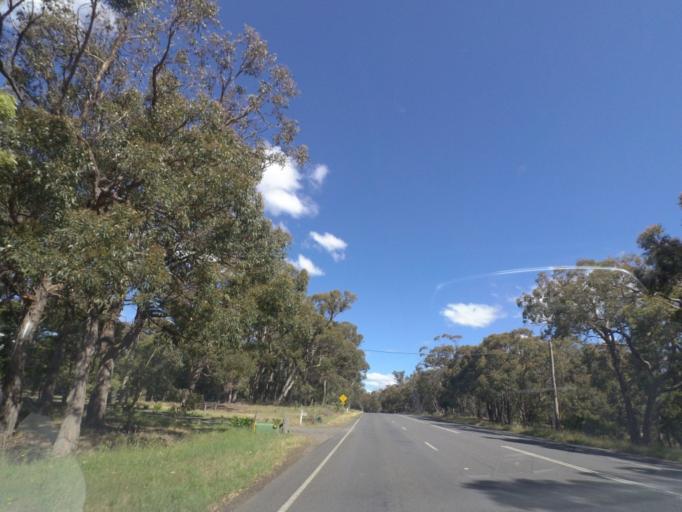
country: AU
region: Victoria
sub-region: Hume
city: Sunbury
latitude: -37.4460
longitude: 144.5706
